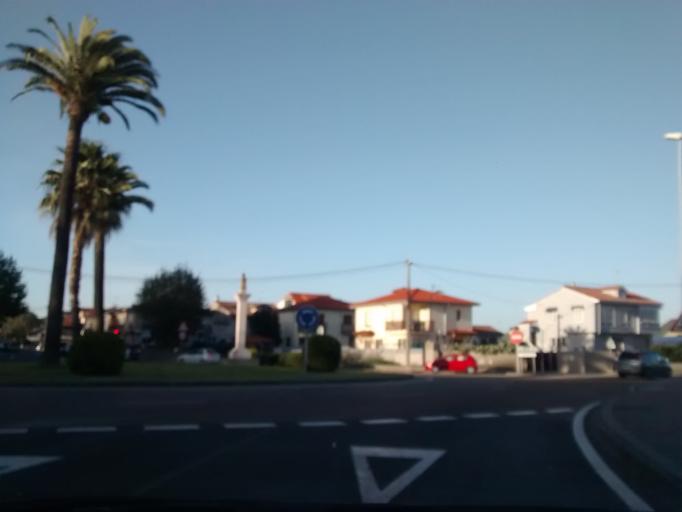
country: ES
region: Cantabria
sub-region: Provincia de Cantabria
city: Santa Cruz de Bezana
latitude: 43.4649
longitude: -3.8672
